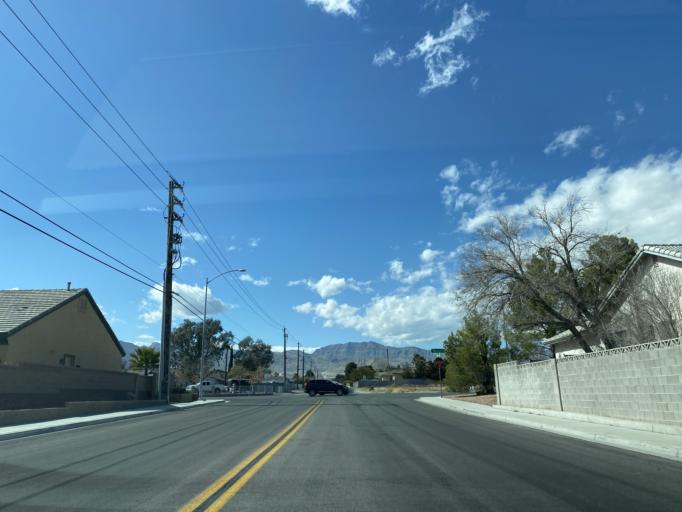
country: US
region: Nevada
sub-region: Clark County
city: Summerlin South
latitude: 36.2556
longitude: -115.2779
